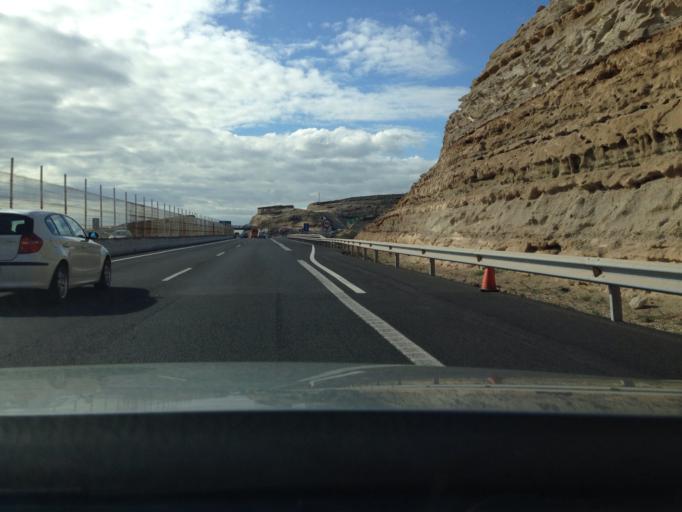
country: ES
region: Canary Islands
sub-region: Provincia de Santa Cruz de Tenerife
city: Fasnia
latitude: 28.2042
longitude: -16.4263
